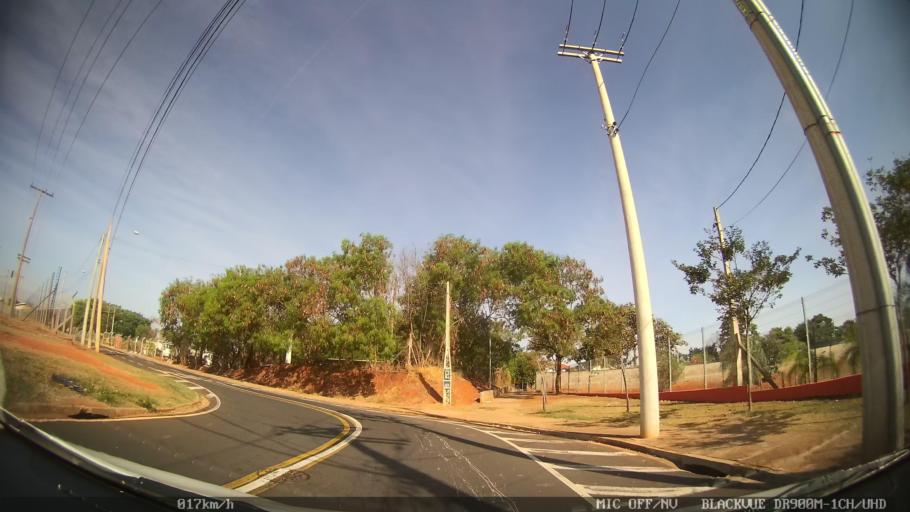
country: BR
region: Sao Paulo
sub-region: Sao Jose Do Rio Preto
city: Sao Jose do Rio Preto
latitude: -20.7884
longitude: -49.3816
